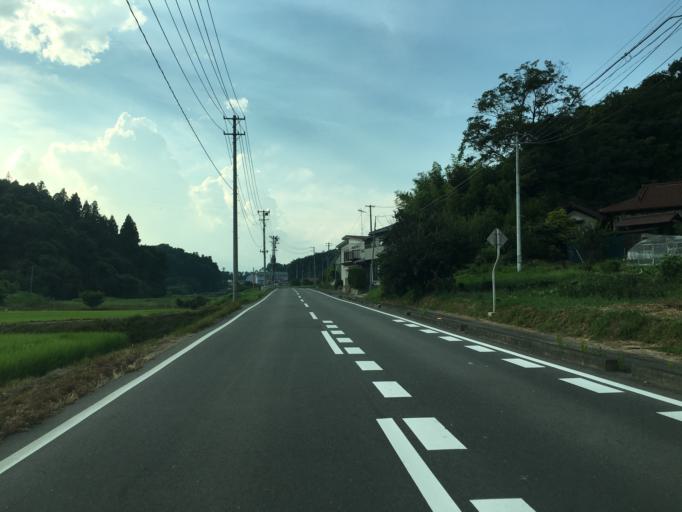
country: JP
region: Fukushima
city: Nihommatsu
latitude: 37.5701
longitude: 140.4354
